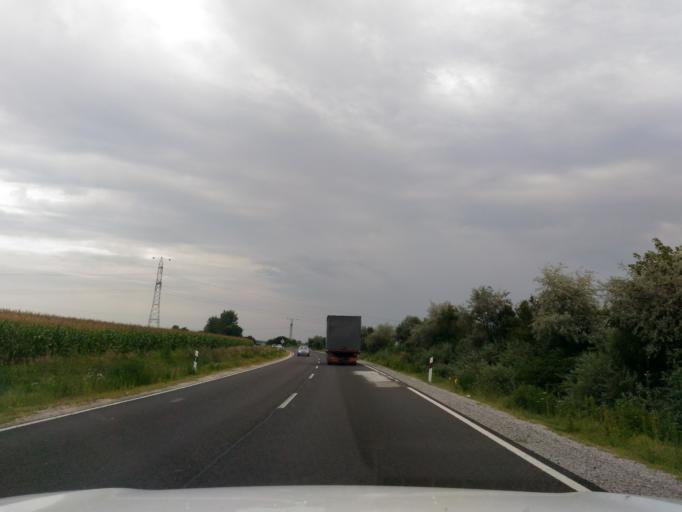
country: HU
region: Jasz-Nagykun-Szolnok
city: Toszeg
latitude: 47.1621
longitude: 20.1073
